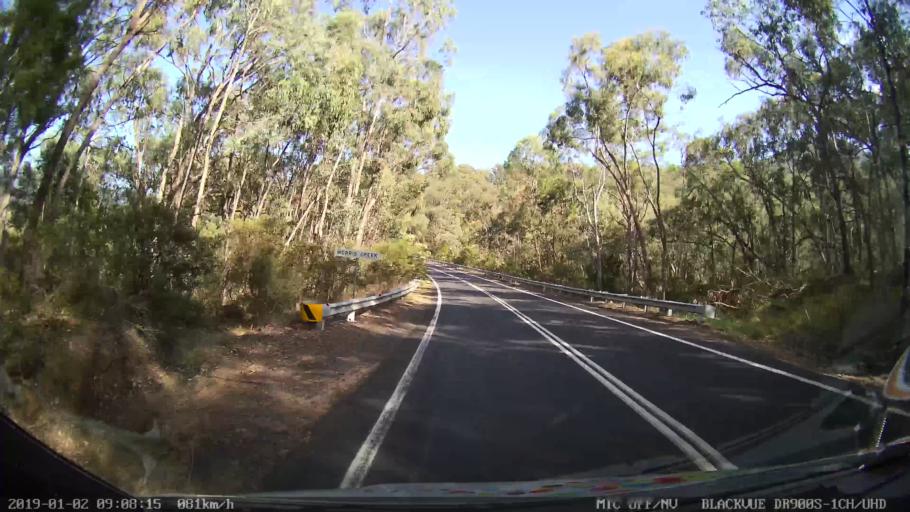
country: AU
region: New South Wales
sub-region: Tumut Shire
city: Tumut
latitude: -35.5320
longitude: 148.2940
